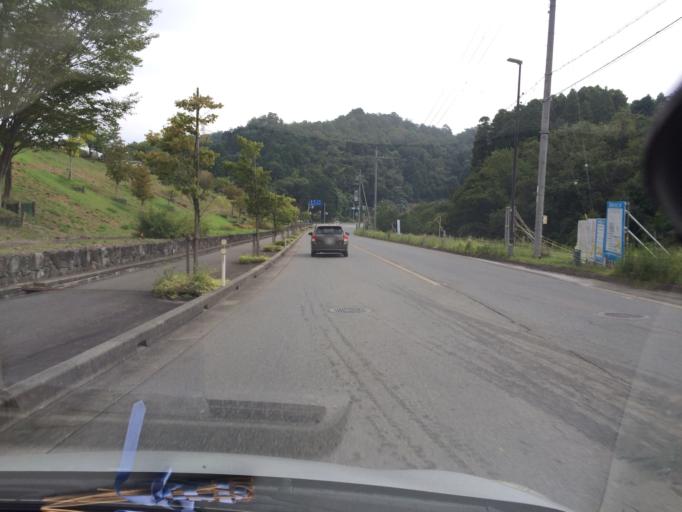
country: JP
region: Hyogo
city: Toyooka
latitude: 35.5252
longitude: 134.8071
